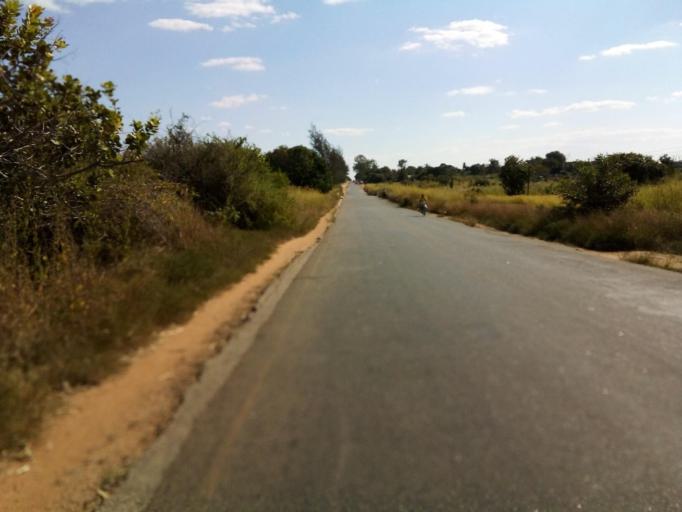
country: MZ
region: Zambezia
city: Quelimane
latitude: -17.5765
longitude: 36.6476
